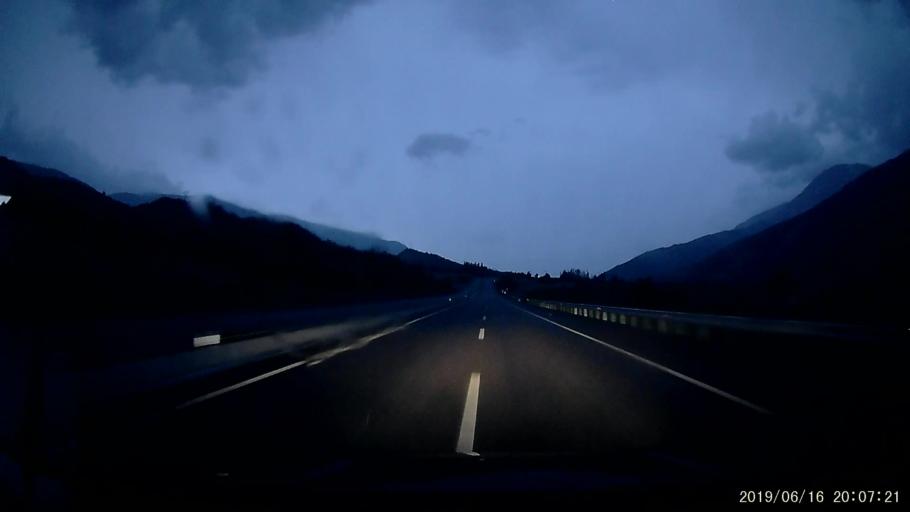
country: TR
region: Sivas
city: Dogansar
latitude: 40.3182
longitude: 37.6260
